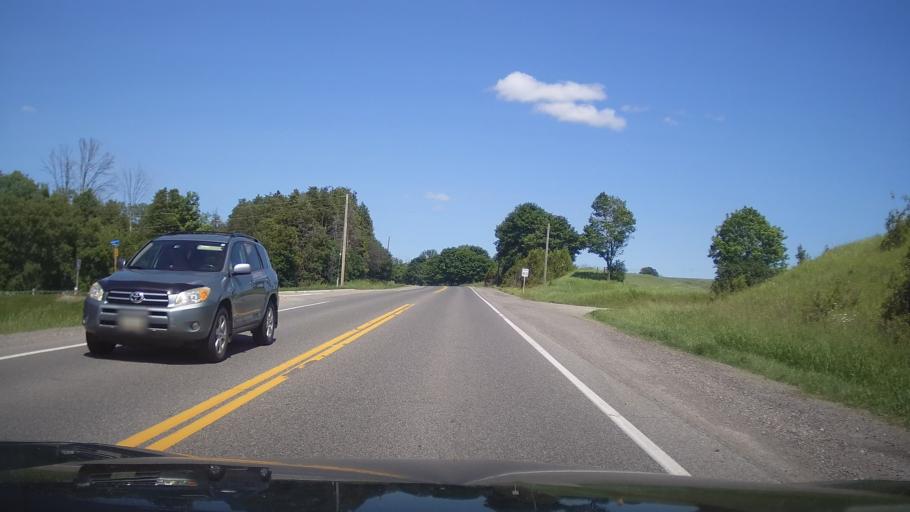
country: CA
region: Ontario
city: Oshawa
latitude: 43.9733
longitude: -78.8761
